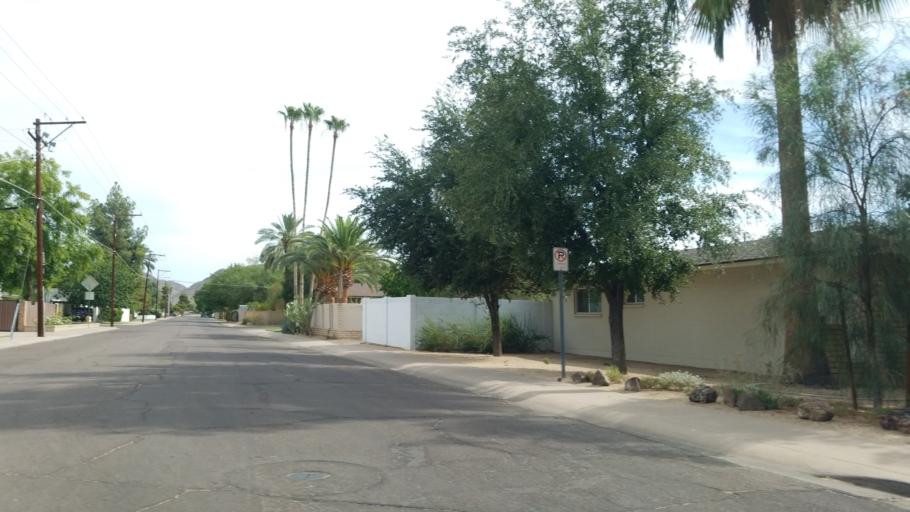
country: US
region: Arizona
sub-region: Maricopa County
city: Glendale
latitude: 33.5604
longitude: -112.0782
